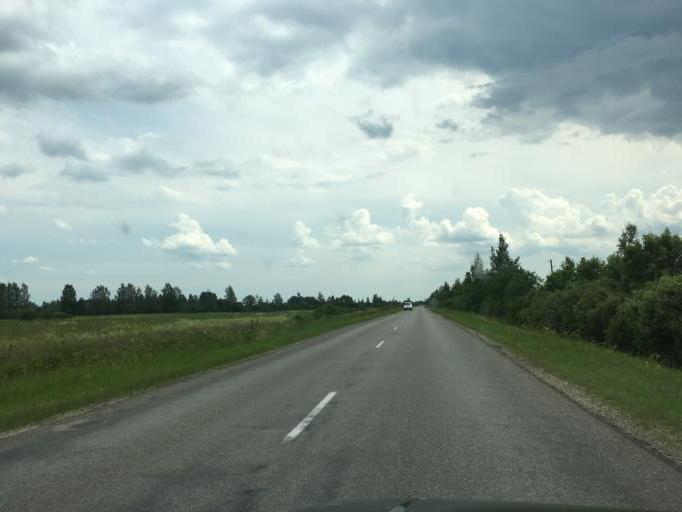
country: LV
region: Rugaju
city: Rugaji
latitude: 56.9284
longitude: 27.0683
